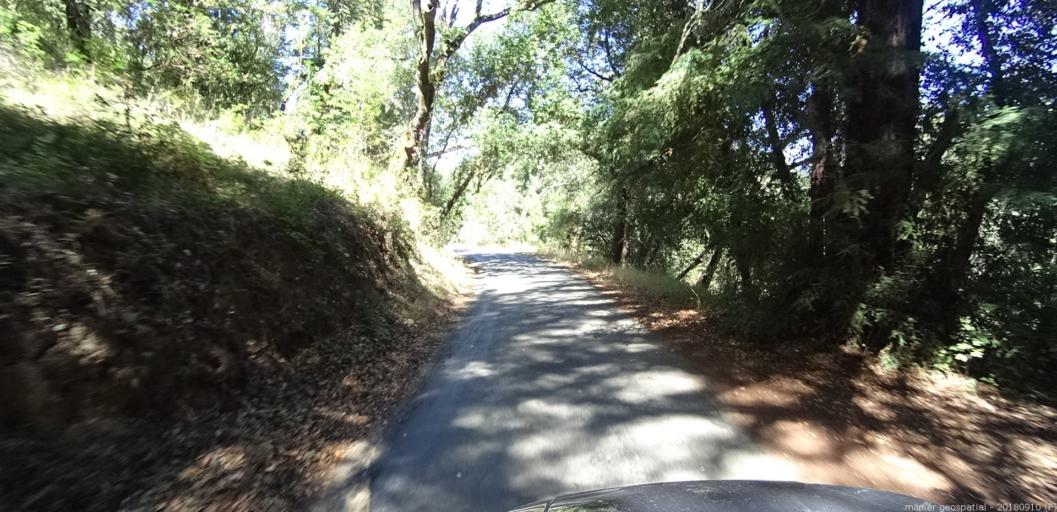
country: US
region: California
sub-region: Monterey County
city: Carmel Valley Village
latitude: 36.4269
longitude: -121.7873
